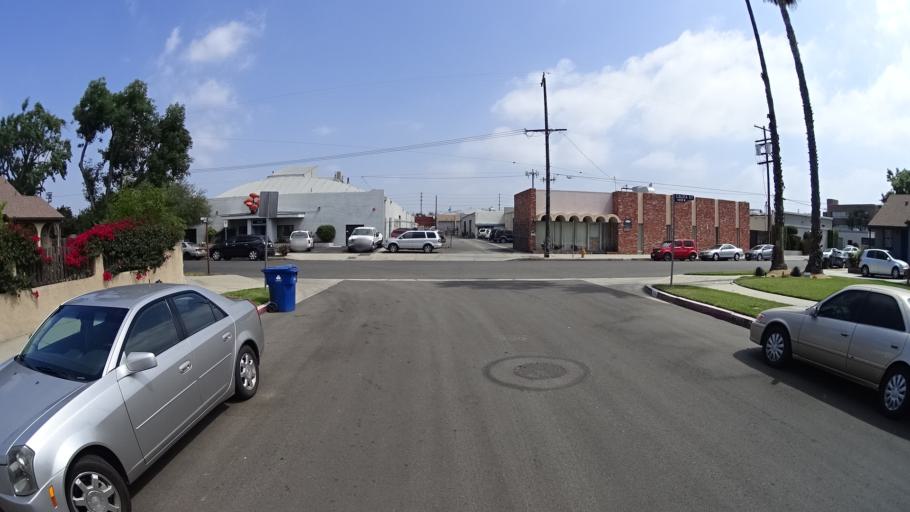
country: US
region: California
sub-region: Los Angeles County
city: Van Nuys
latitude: 34.1773
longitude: -118.4608
